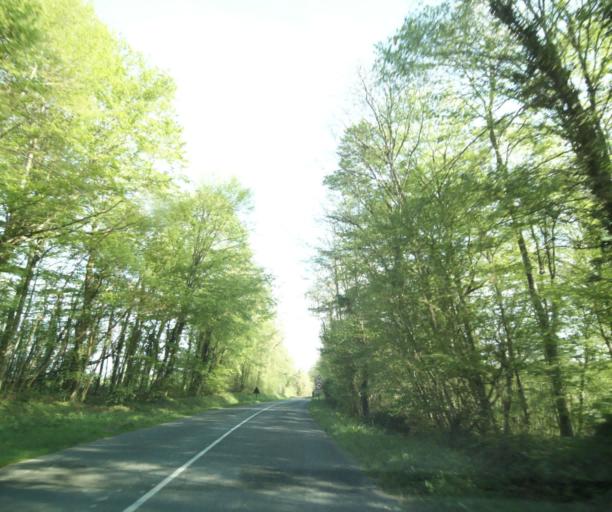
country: FR
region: Ile-de-France
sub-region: Departement de Seine-et-Marne
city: Vernou-la-Celle-sur-Seine
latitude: 48.4512
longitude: 2.8594
